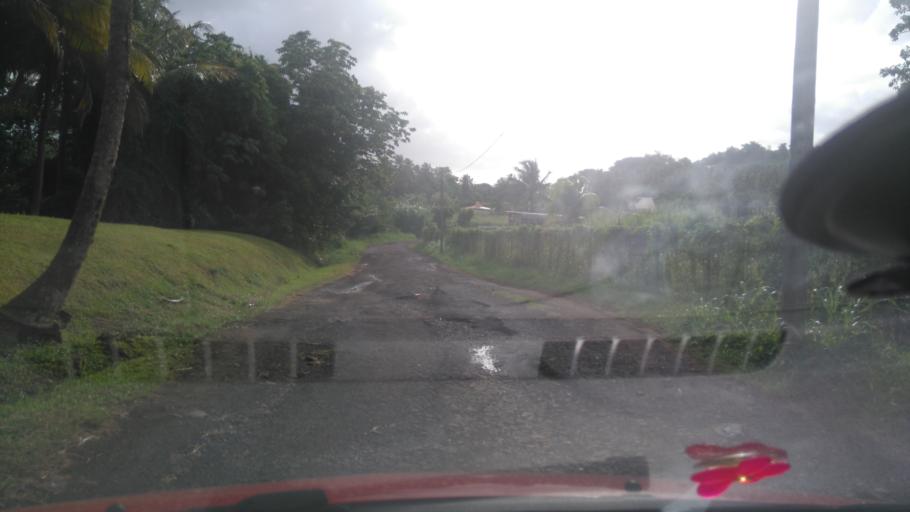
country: MQ
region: Martinique
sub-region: Martinique
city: Ducos
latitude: 14.5524
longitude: -60.9643
